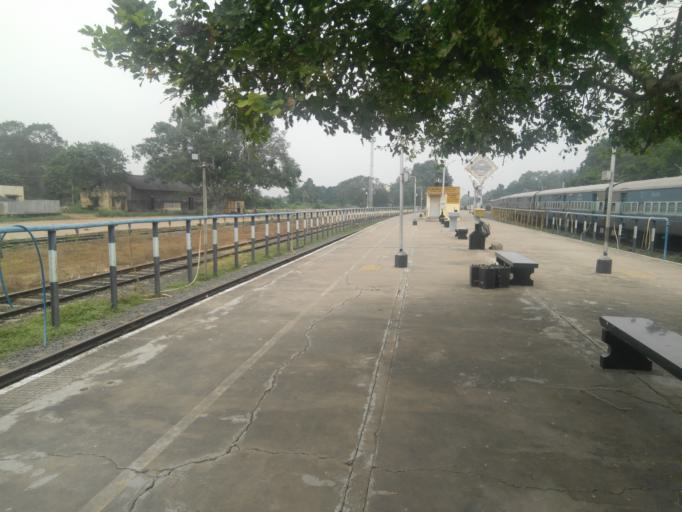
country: IN
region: Tamil Nadu
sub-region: Nagapattinam
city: Mayiladuthurai
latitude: 11.0958
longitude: 79.6283
